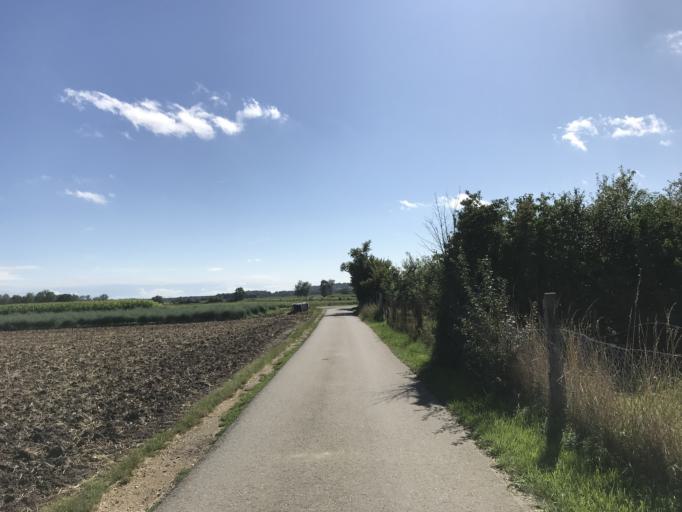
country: DE
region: Baden-Wuerttemberg
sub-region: Tuebingen Region
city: Langenau
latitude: 48.4845
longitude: 10.1270
